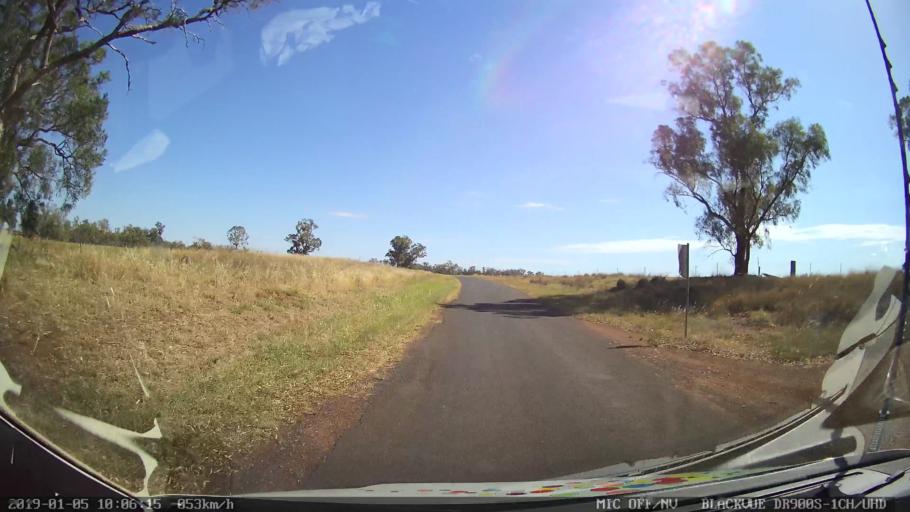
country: AU
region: New South Wales
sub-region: Gilgandra
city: Gilgandra
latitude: -31.6596
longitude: 148.8693
